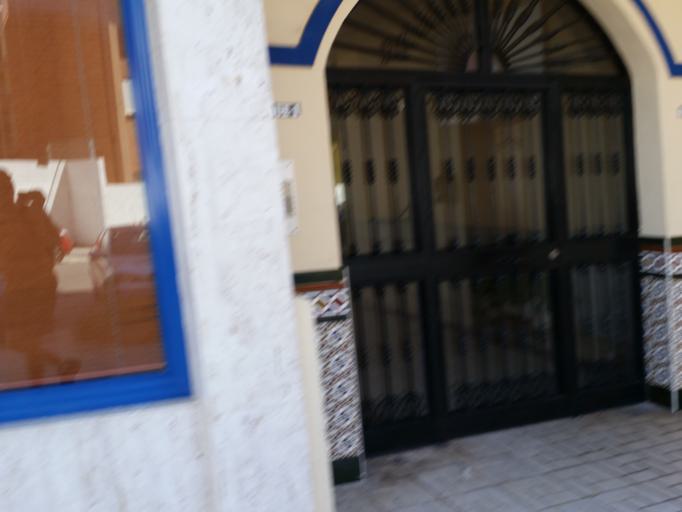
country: ES
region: Andalusia
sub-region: Provincia de Malaga
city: Fuengirola
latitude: 36.5326
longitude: -4.6286
